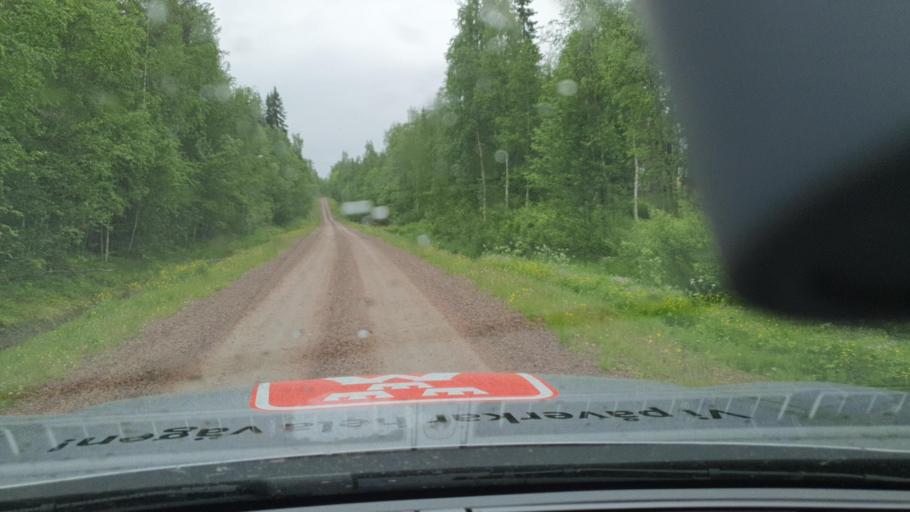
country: SE
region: Norrbotten
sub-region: Overkalix Kommun
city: OEverkalix
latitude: 66.5221
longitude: 22.7442
